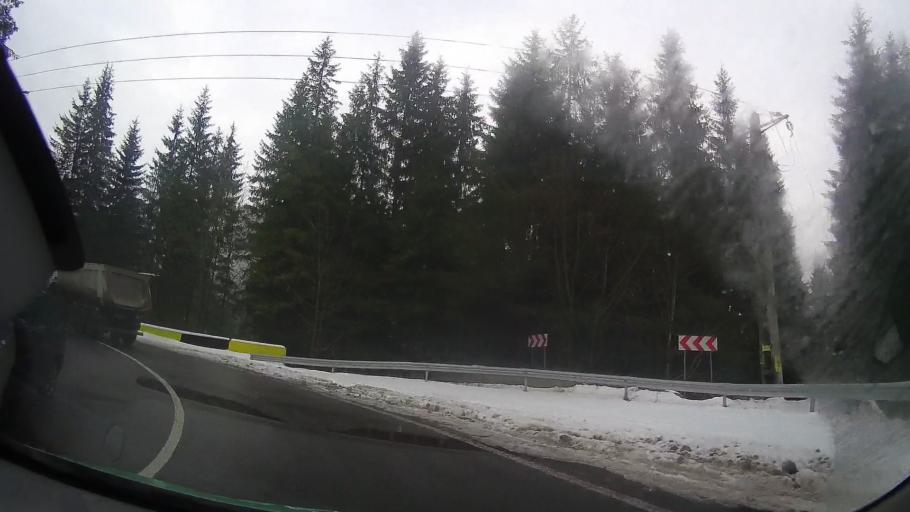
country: RO
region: Neamt
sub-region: Comuna Bicaz Chei
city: Bicaz Chei
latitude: 46.7816
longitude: 25.7836
